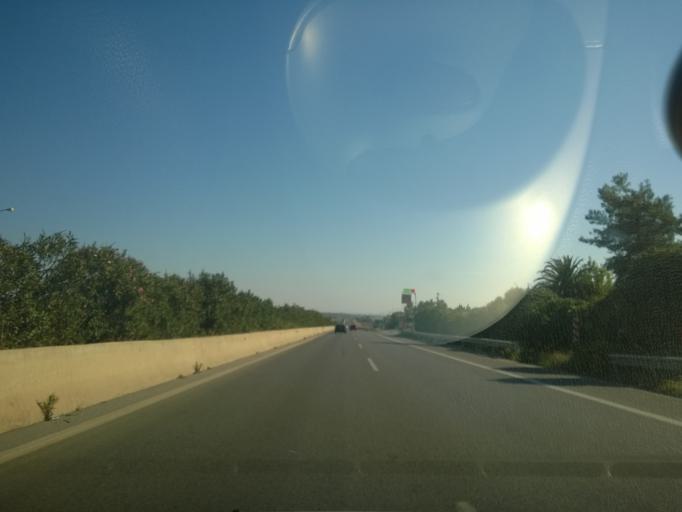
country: GR
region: Central Macedonia
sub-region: Nomos Chalkidikis
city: Lakkoma
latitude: 40.3874
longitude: 23.0371
